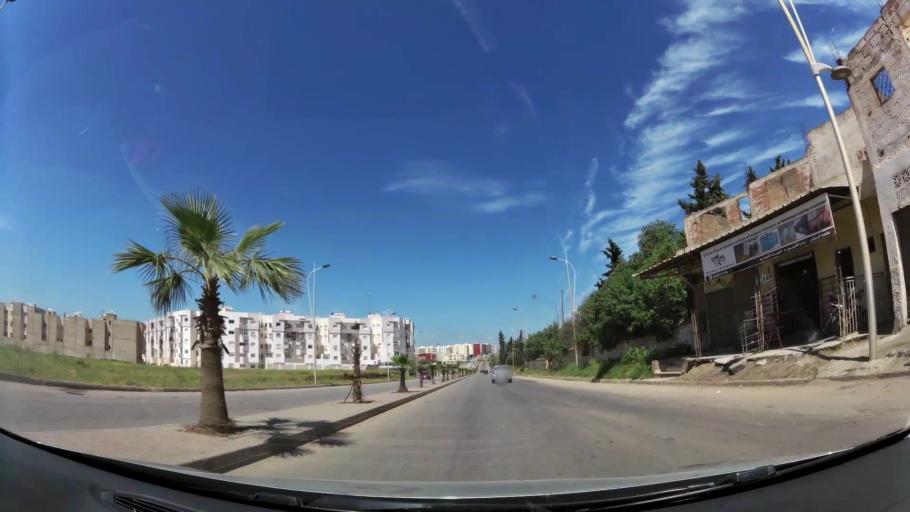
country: MA
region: Fes-Boulemane
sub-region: Fes
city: Fes
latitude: 33.9966
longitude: -4.9840
